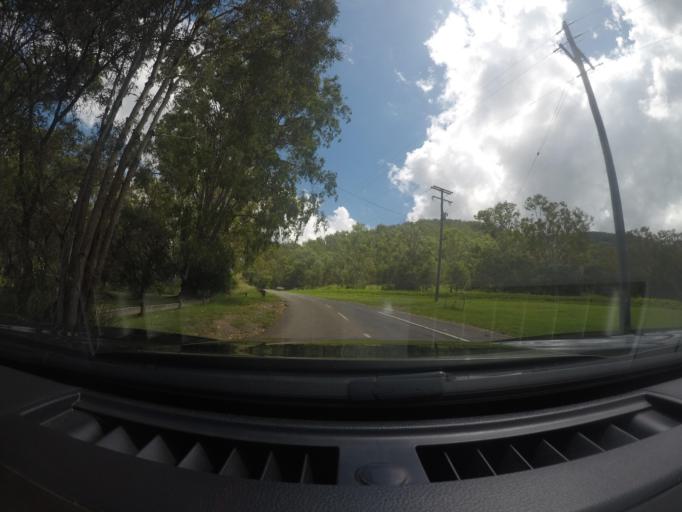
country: AU
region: Queensland
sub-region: Moreton Bay
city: Woodford
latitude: -27.1035
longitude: 152.5608
